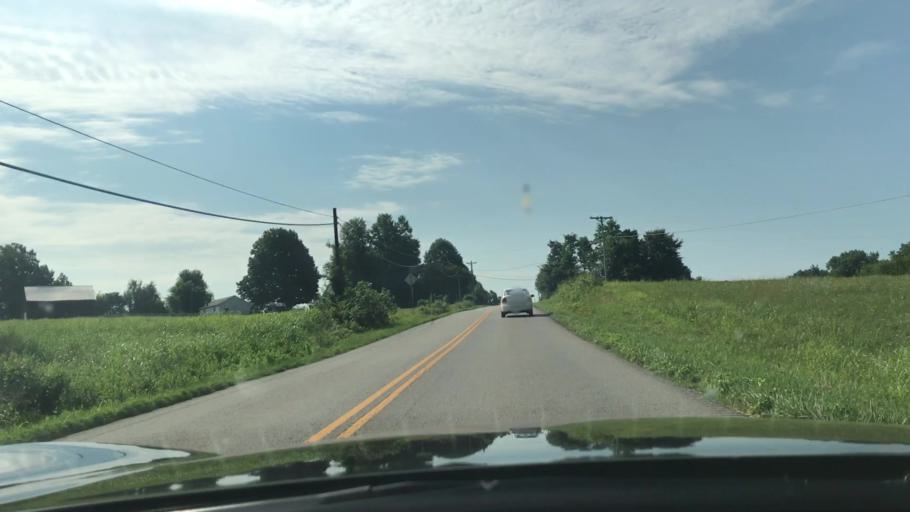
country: US
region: Kentucky
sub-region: Green County
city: Greensburg
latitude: 37.2662
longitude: -85.5625
